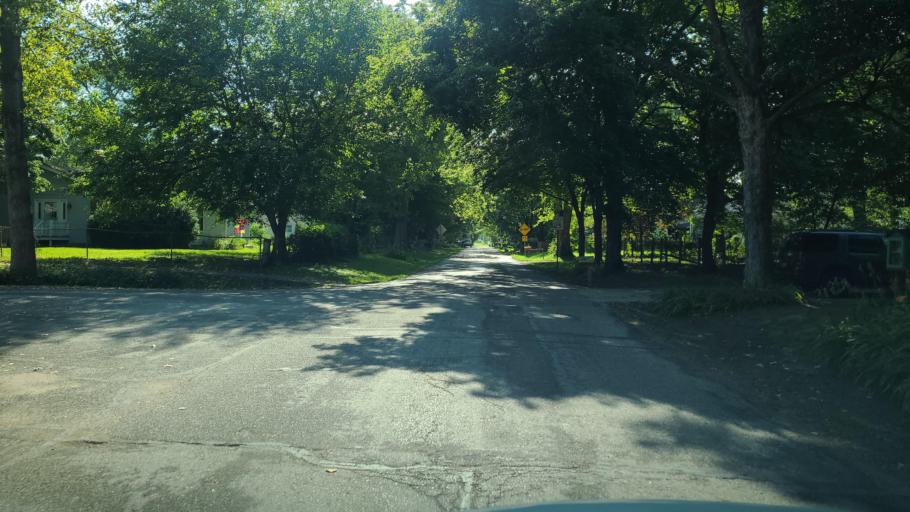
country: US
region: Kansas
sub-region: Douglas County
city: Lawrence
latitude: 38.9806
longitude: -95.2311
